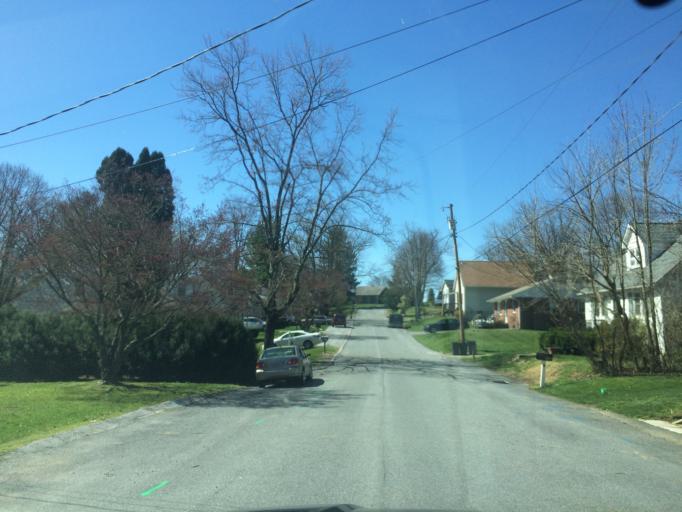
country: US
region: Maryland
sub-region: Carroll County
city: Westminster
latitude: 39.5695
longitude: -77.0001
